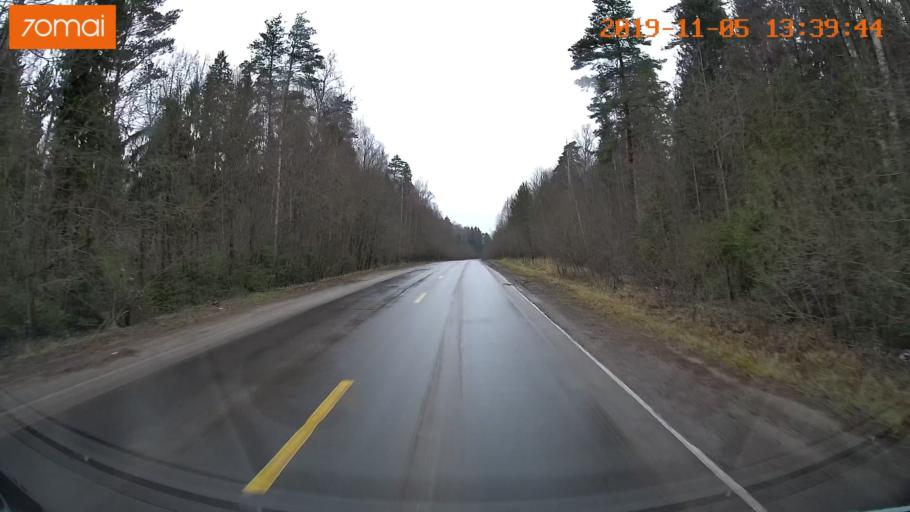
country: RU
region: Ivanovo
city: Shuya
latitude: 56.9426
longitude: 41.3849
